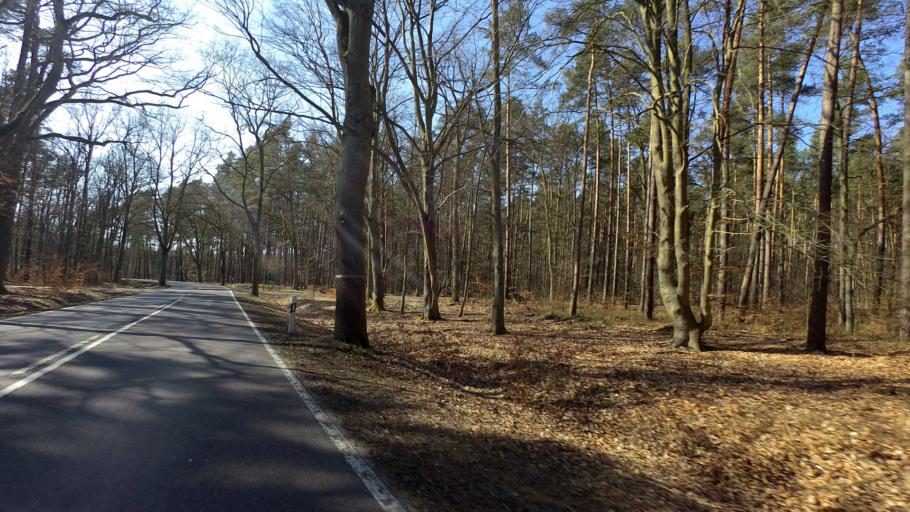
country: DE
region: Brandenburg
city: Oranienburg
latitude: 52.7944
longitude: 13.2069
